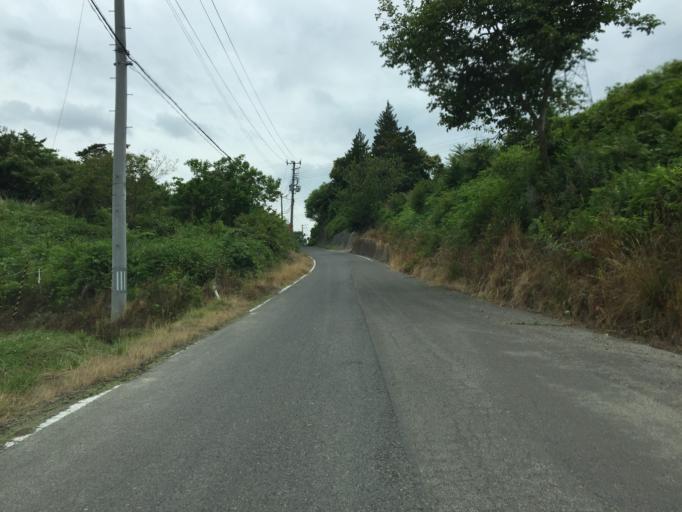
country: JP
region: Fukushima
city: Miharu
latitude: 37.3987
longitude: 140.5361
